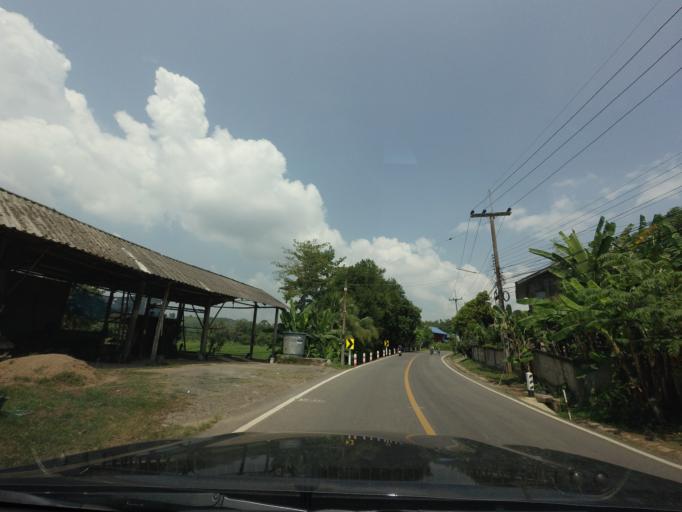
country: TH
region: Nan
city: Santi Suk
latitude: 18.9524
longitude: 100.9223
